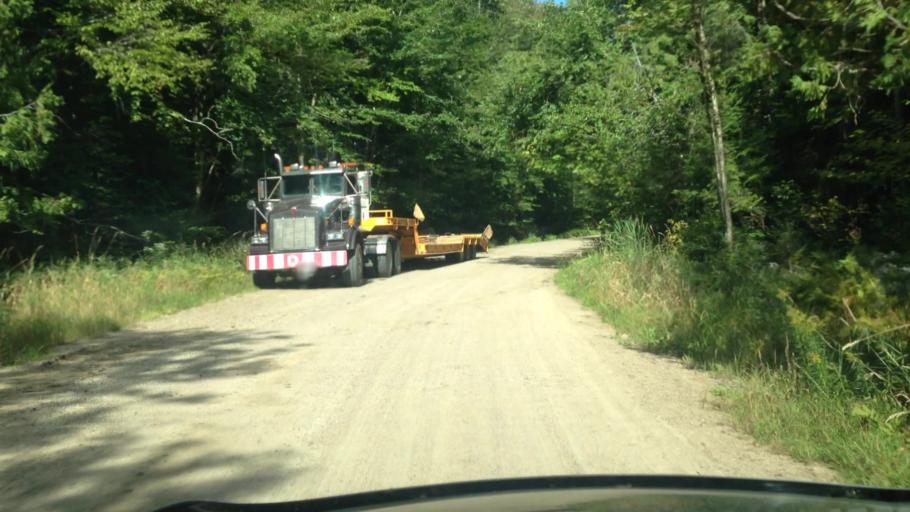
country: CA
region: Quebec
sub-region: Laurentides
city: Mont-Tremblant
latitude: 45.9235
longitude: -74.5822
